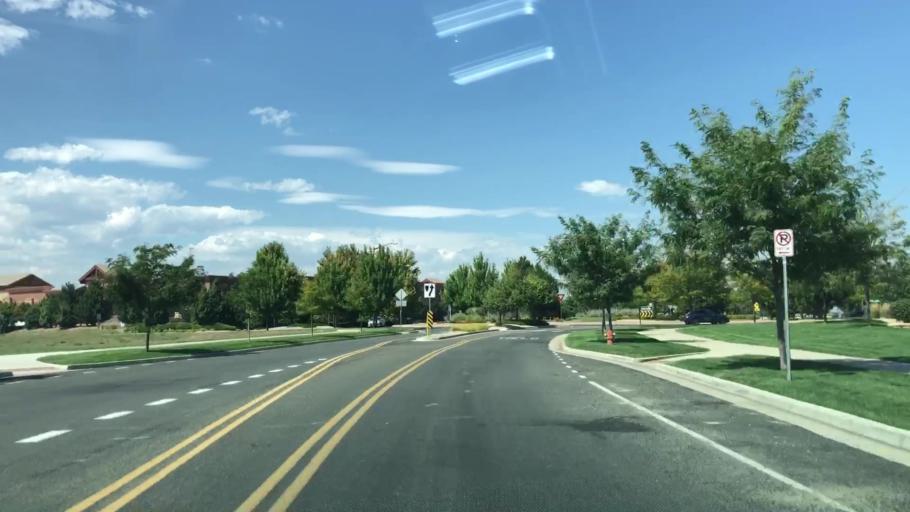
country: US
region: Colorado
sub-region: Larimer County
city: Loveland
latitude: 40.4036
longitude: -105.0347
